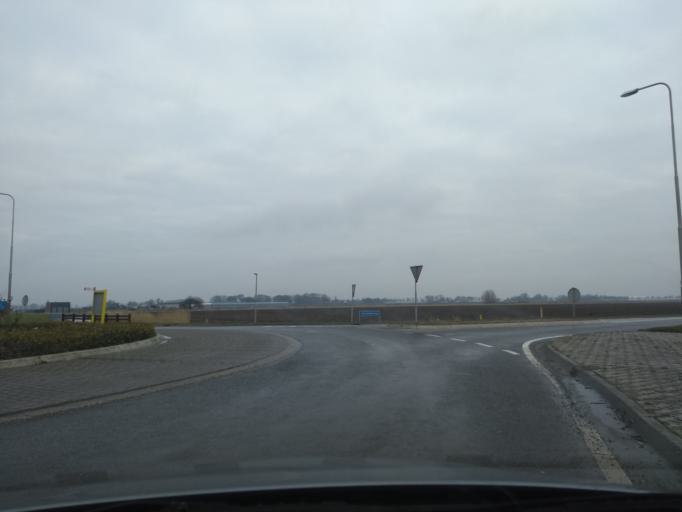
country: NL
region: Overijssel
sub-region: Gemeente Steenwijkerland
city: Vollenhove
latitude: 52.7104
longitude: 5.8757
